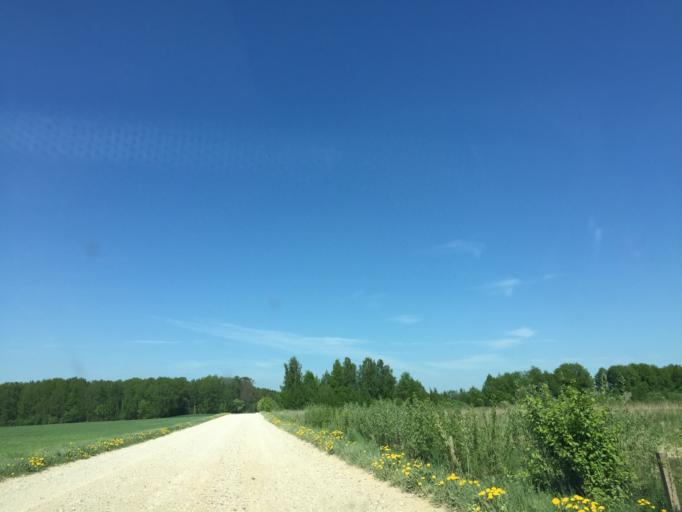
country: LV
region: Ikskile
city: Ikskile
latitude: 56.8726
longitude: 24.4998
